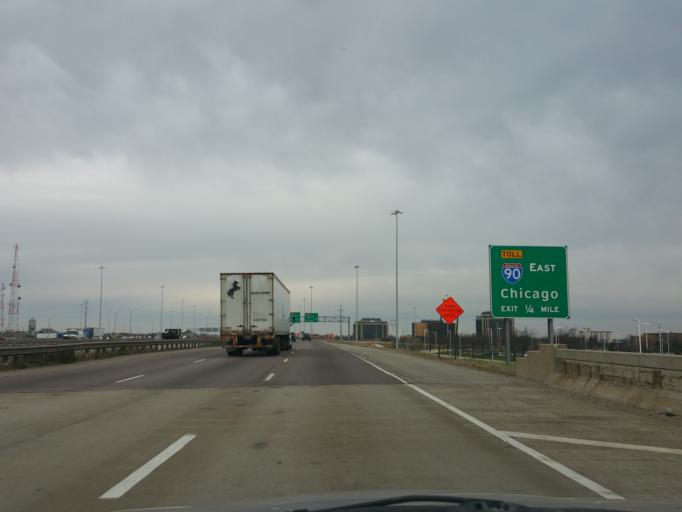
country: US
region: Illinois
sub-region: Cook County
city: Rolling Meadows
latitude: 42.0506
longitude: -88.0286
